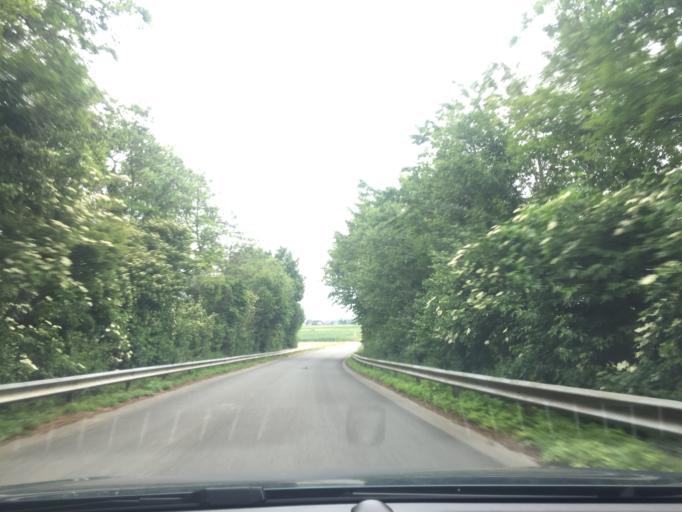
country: BE
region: Wallonia
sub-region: Province du Hainaut
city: Pecq
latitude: 50.6543
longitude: 3.2948
